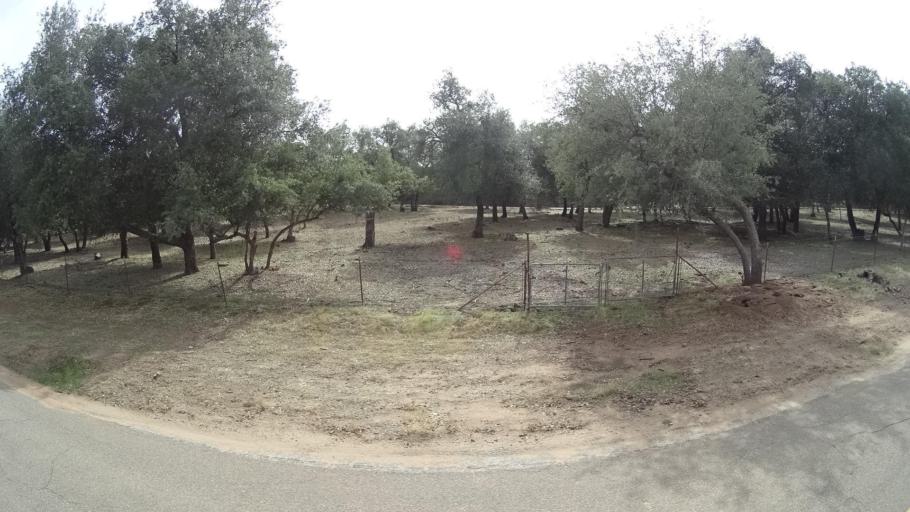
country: US
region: California
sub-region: San Diego County
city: Descanso
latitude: 32.8620
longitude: -116.6360
